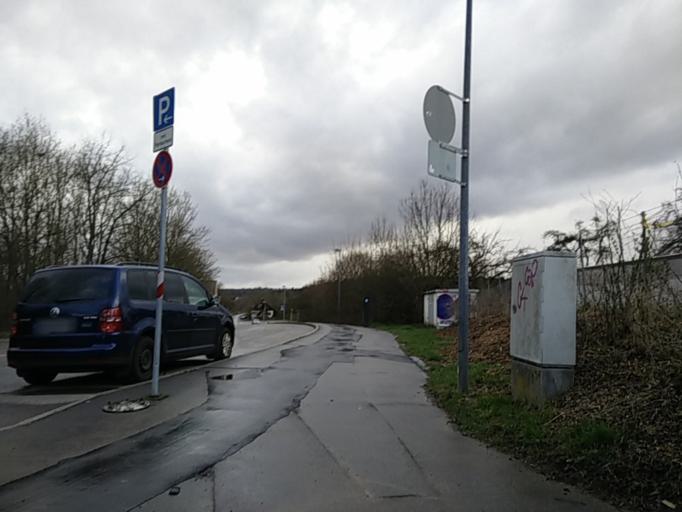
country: DE
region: Baden-Wuerttemberg
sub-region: Tuebingen Region
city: Tuebingen
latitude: 48.5389
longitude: 9.0296
